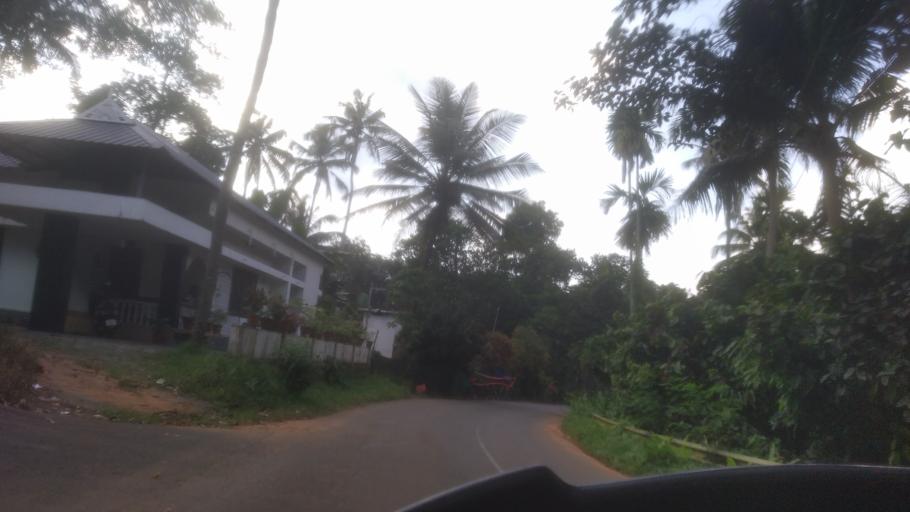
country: IN
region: Kerala
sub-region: Ernakulam
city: Kotamangalam
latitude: 10.0034
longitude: 76.6610
